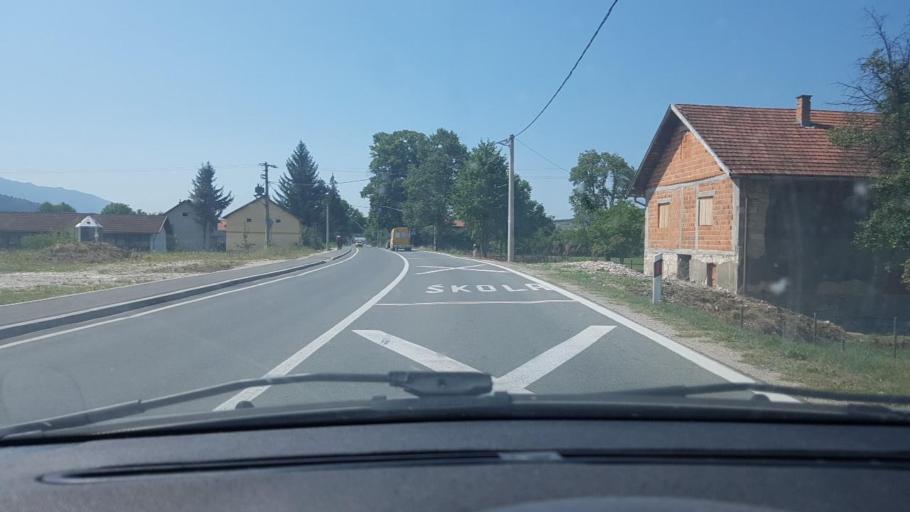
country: BA
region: Federation of Bosnia and Herzegovina
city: Bihac
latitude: 44.7919
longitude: 15.9273
